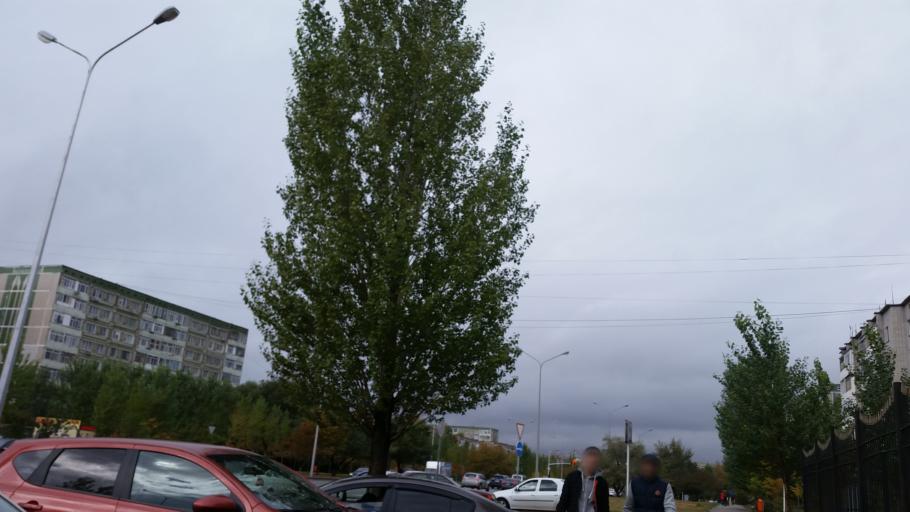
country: KZ
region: Astana Qalasy
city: Astana
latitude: 51.1505
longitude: 71.4823
